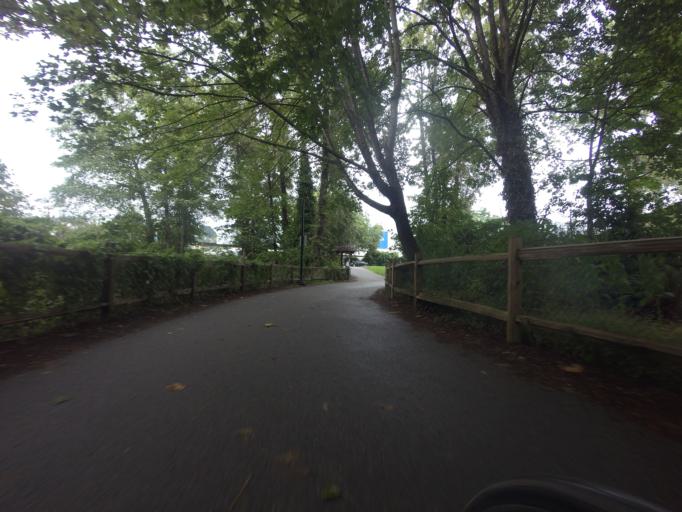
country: CA
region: British Columbia
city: West End
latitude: 49.3236
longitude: -123.1395
